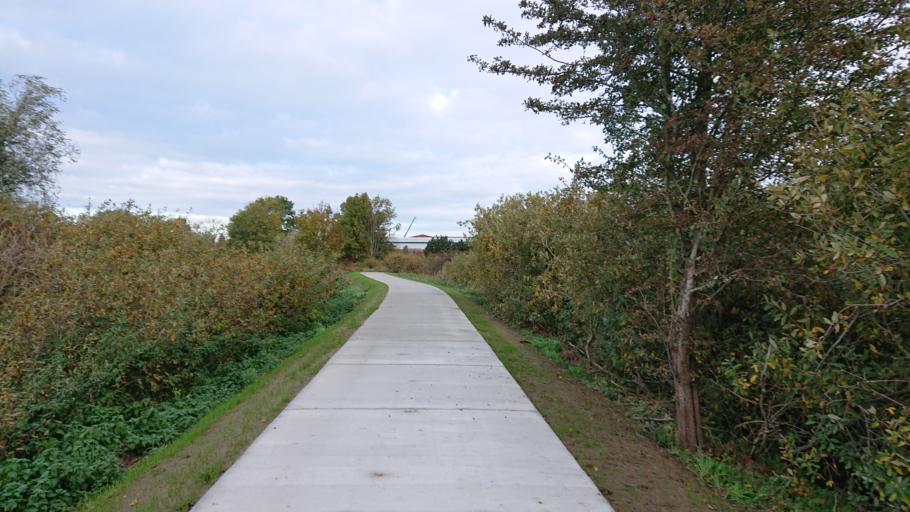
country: DE
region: Mecklenburg-Vorpommern
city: Barth
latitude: 54.3664
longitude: 12.7408
